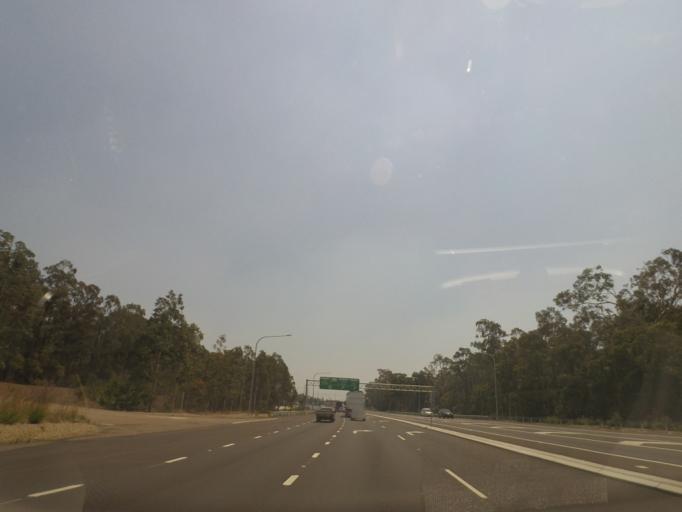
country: AU
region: New South Wales
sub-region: Newcastle
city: Beresfield
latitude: -32.8168
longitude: 151.6355
